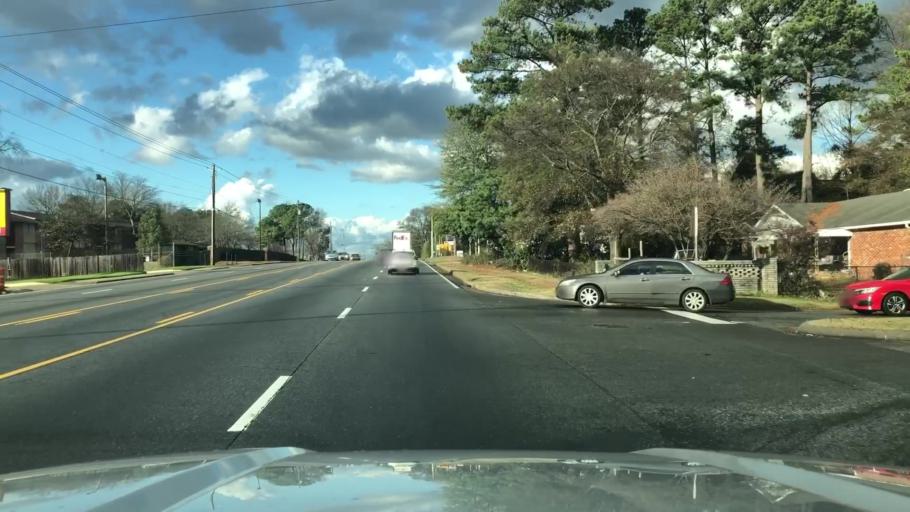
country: US
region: Georgia
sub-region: Clayton County
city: Riverdale
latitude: 33.6090
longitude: -84.4361
